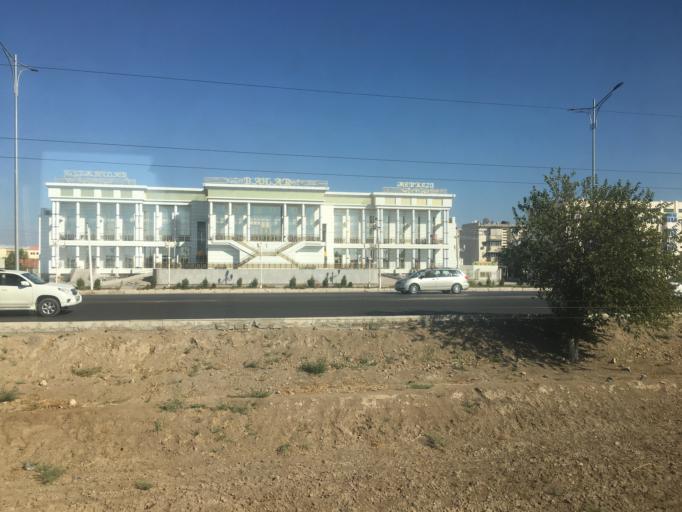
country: TM
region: Lebap
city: Turkmenabat
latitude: 39.0372
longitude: 63.5731
